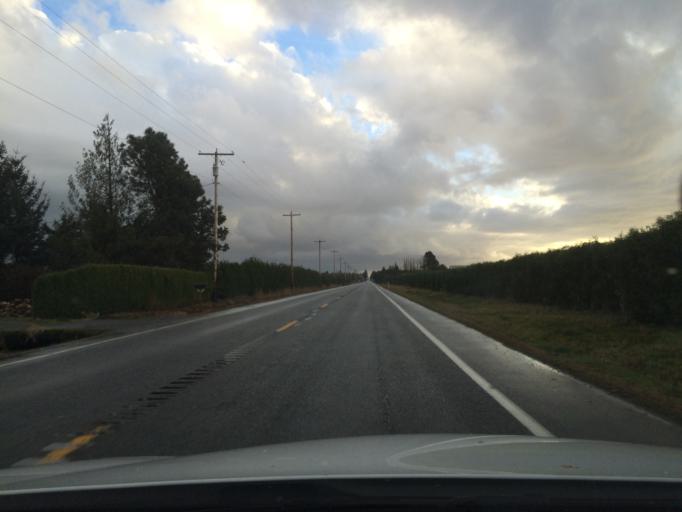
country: US
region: Washington
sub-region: Whatcom County
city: Lynden
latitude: 48.9585
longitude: -122.4852
